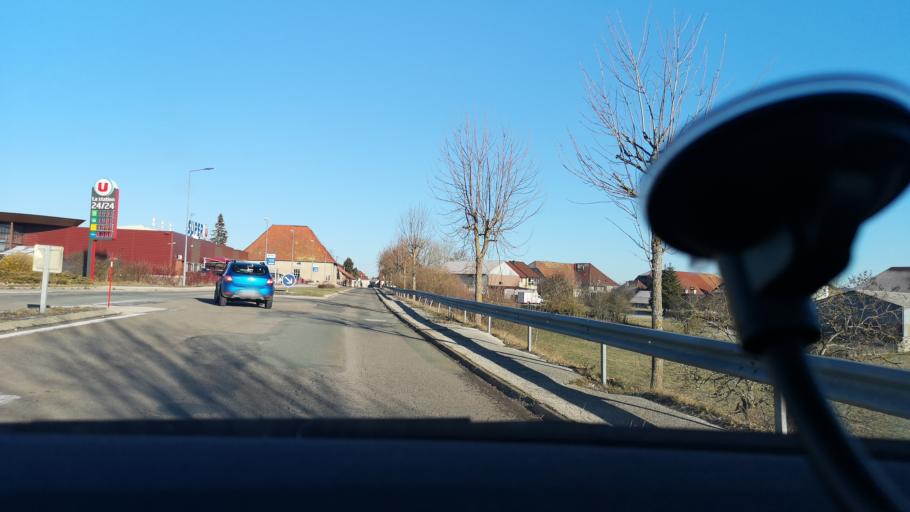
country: FR
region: Franche-Comte
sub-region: Departement du Doubs
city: Frasne
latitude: 46.8521
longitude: 6.1517
